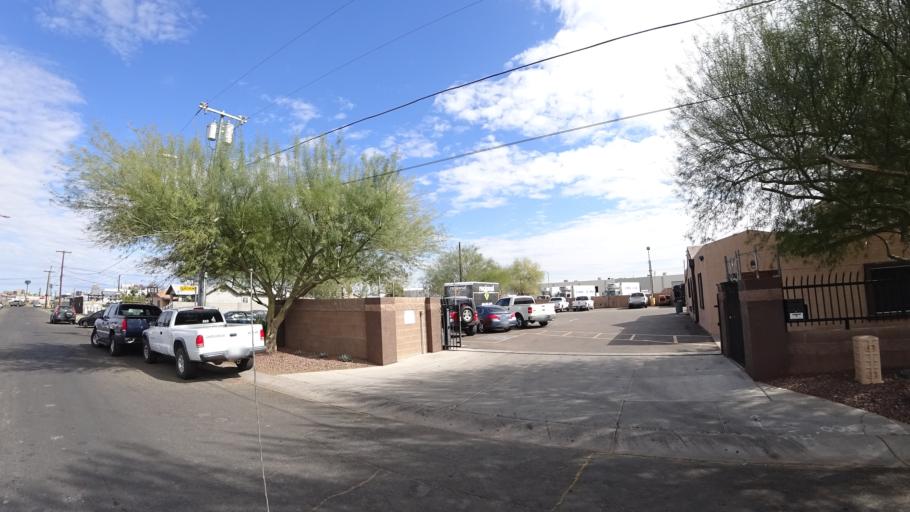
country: US
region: Arizona
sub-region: Maricopa County
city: Phoenix
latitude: 33.4246
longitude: -112.0813
